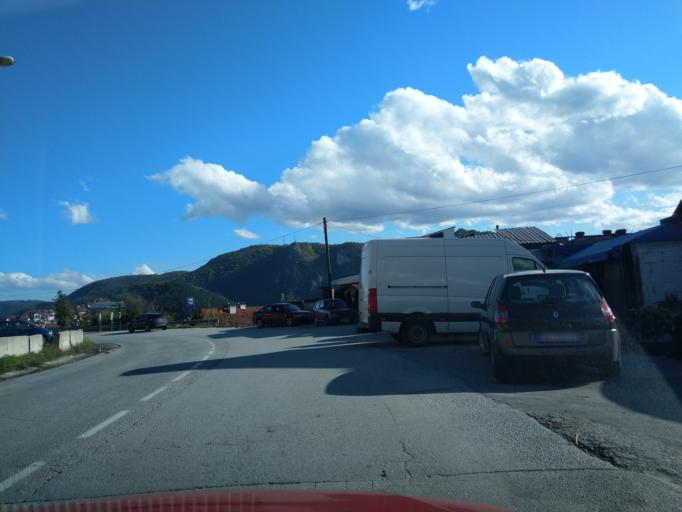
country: RS
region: Central Serbia
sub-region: Zlatiborski Okrug
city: Uzice
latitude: 43.8623
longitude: 19.8167
